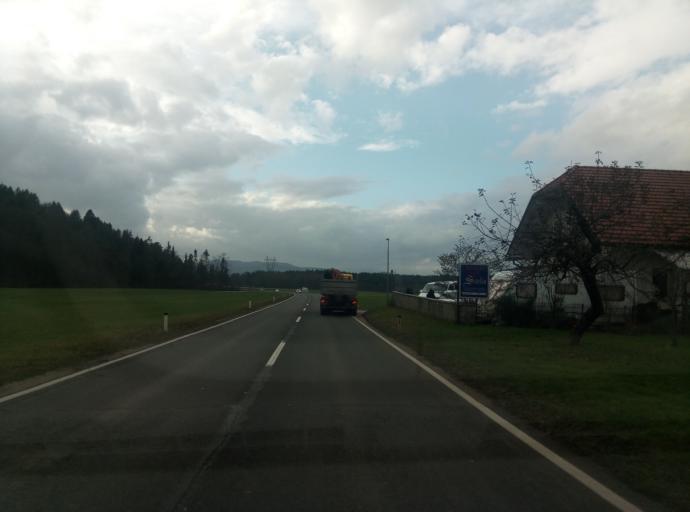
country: SI
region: Domzale
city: Dob
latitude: 46.1616
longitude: 14.6556
